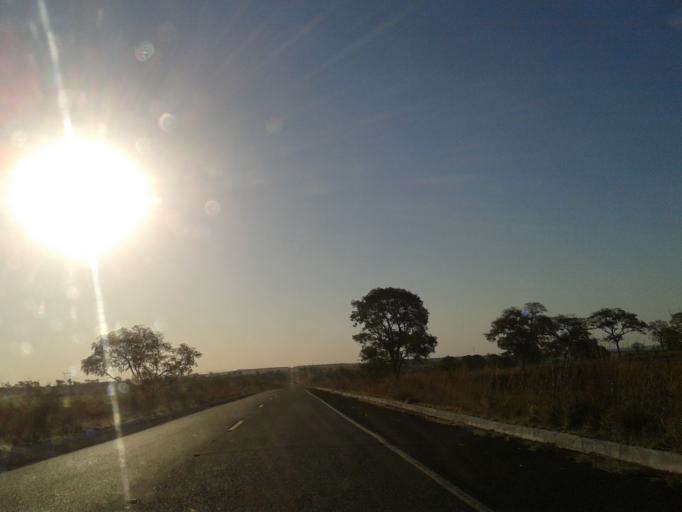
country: BR
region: Minas Gerais
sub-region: Santa Vitoria
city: Santa Vitoria
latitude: -19.0836
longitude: -50.3551
